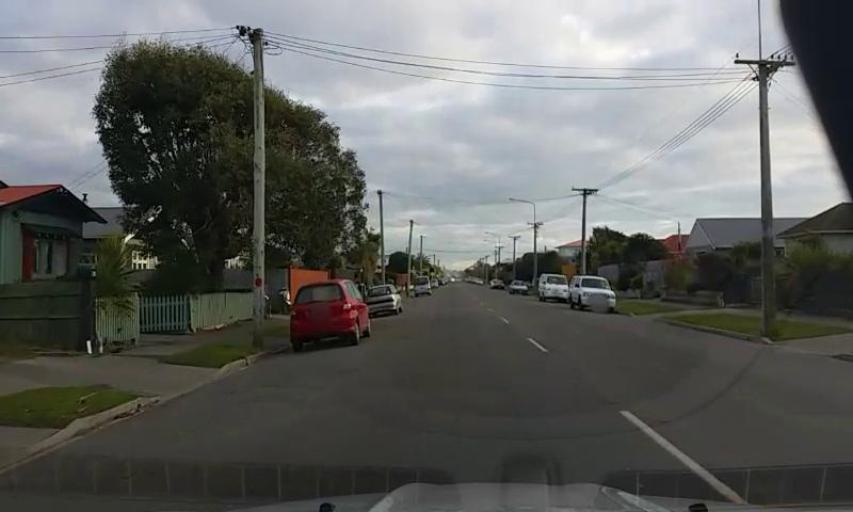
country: NZ
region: Canterbury
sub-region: Christchurch City
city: Christchurch
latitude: -43.5291
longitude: 172.7352
